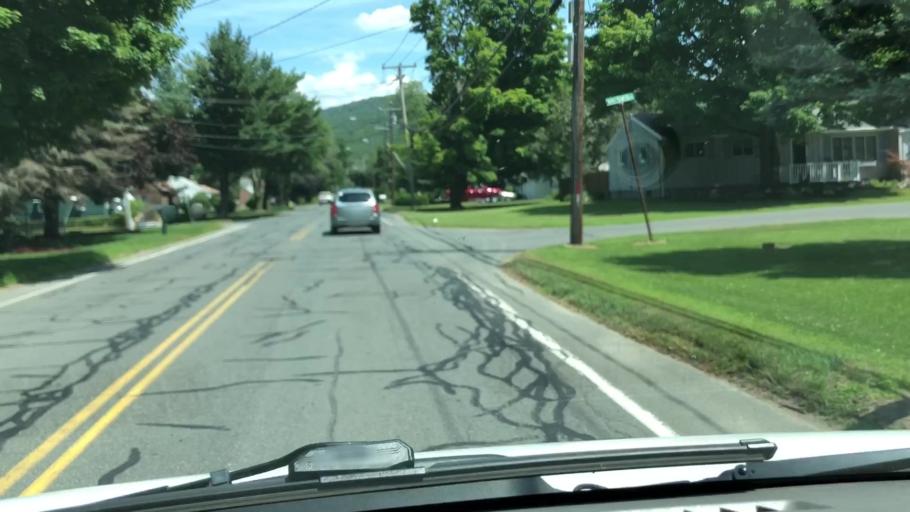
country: US
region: Massachusetts
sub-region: Berkshire County
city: Dalton
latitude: 42.4524
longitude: -73.1961
